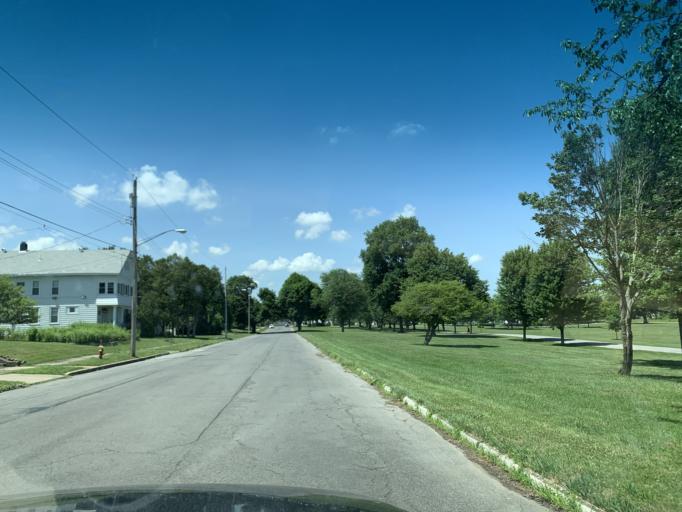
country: US
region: New York
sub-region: Oneida County
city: Utica
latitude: 43.0861
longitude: -75.1971
